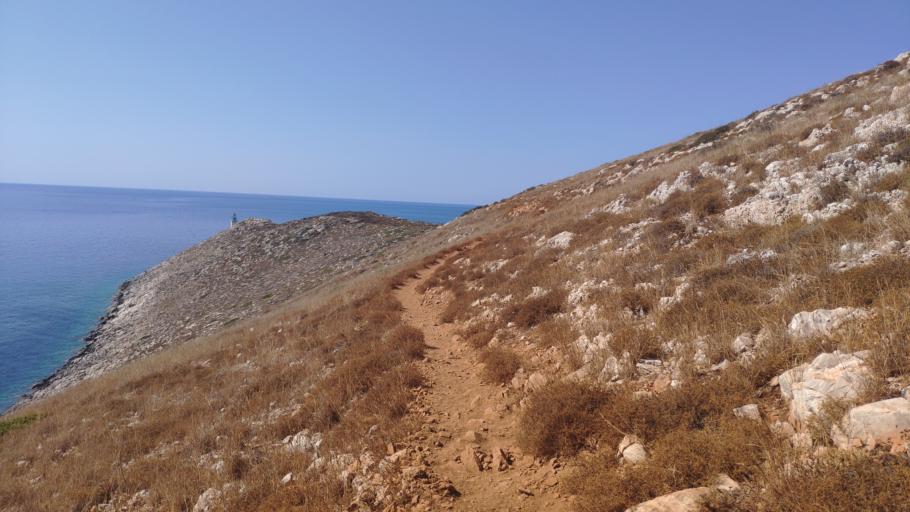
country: GR
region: Peloponnese
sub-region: Nomos Lakonias
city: Gytheio
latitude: 36.3912
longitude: 22.4835
